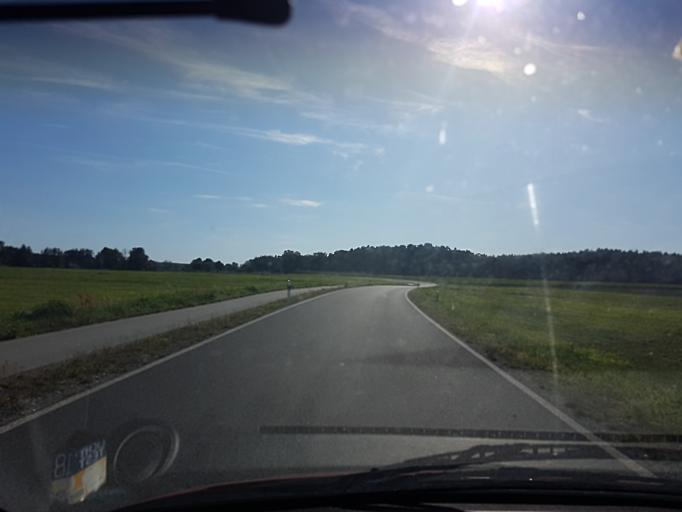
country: DE
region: Bavaria
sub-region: Upper Franconia
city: Hallerndorf
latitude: 49.7430
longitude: 10.9546
